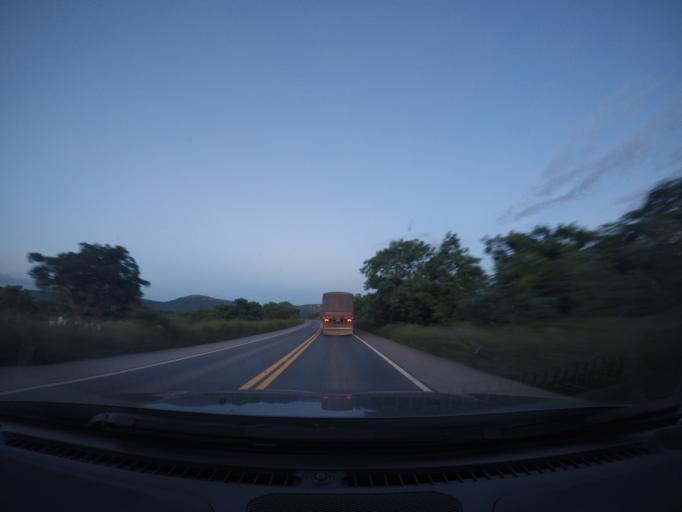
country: BR
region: Bahia
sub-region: Seabra
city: Seabra
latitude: -12.4849
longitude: -41.7231
